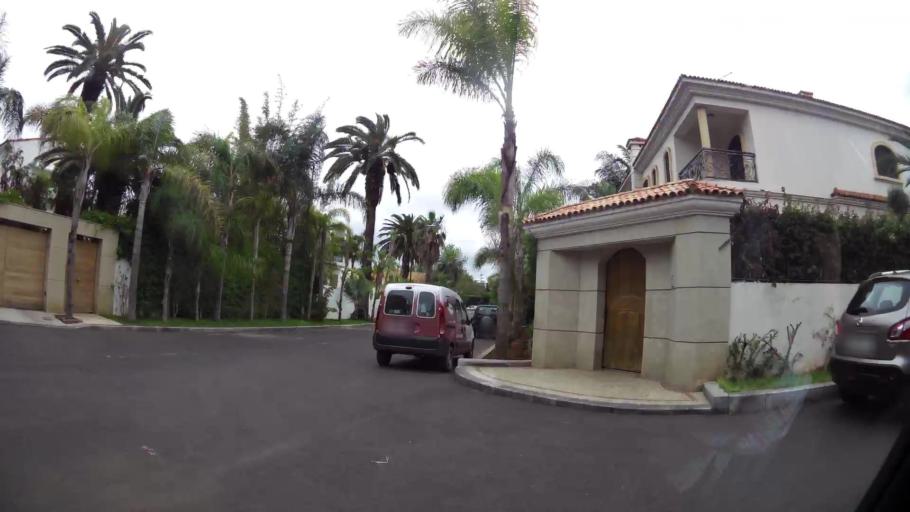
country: MA
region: Grand Casablanca
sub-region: Casablanca
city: Casablanca
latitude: 33.5838
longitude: -7.6613
